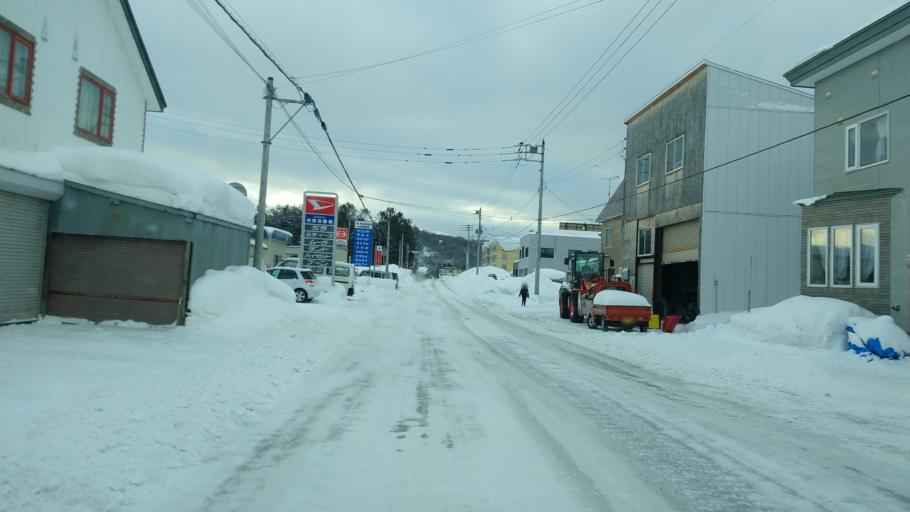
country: JP
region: Hokkaido
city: Niseko Town
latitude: 42.9089
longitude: 140.7554
